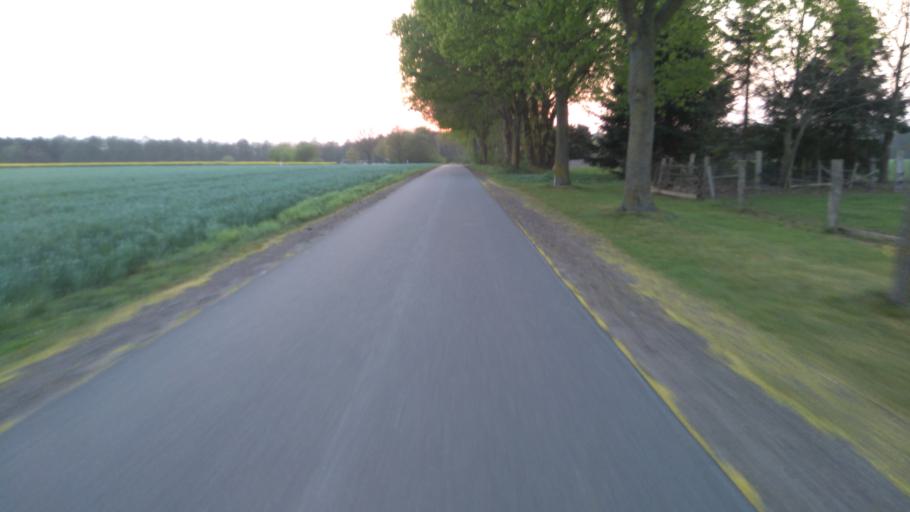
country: DE
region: Lower Saxony
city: Bargstedt
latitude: 53.4700
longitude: 9.4698
